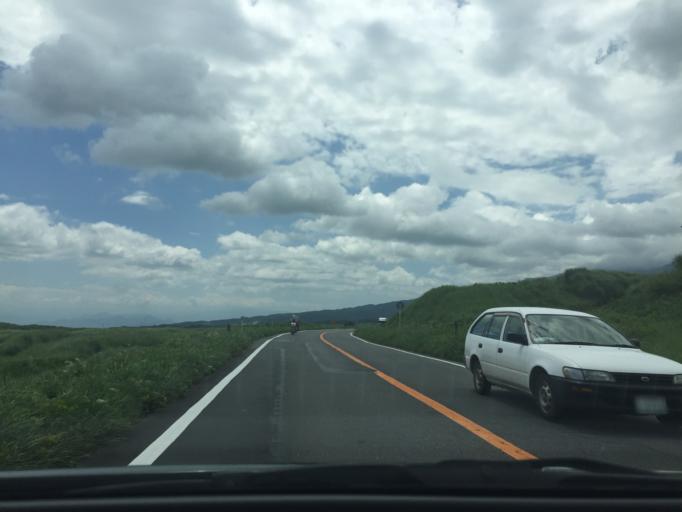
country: JP
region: Shizuoka
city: Gotemba
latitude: 35.2763
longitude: 138.8746
